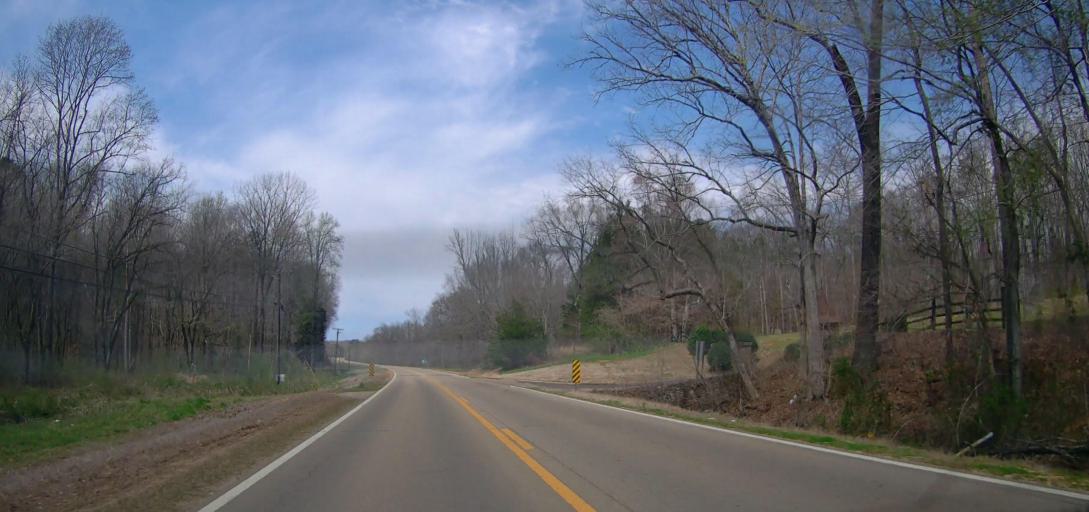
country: US
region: Mississippi
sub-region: Union County
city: New Albany
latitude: 34.4661
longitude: -88.9838
